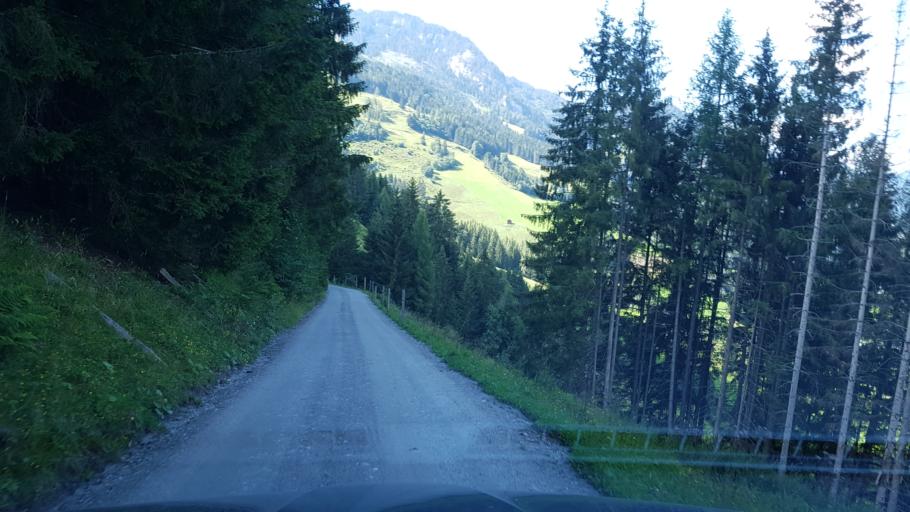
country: AT
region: Salzburg
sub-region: Politischer Bezirk Sankt Johann im Pongau
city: Dorfgastein
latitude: 47.2522
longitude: 13.0818
